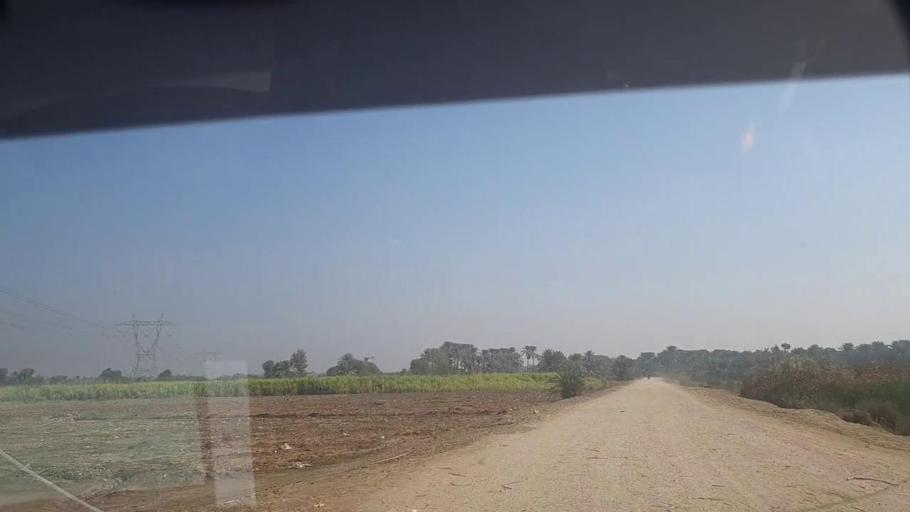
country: PK
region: Sindh
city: Khairpur
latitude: 27.4575
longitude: 68.7488
